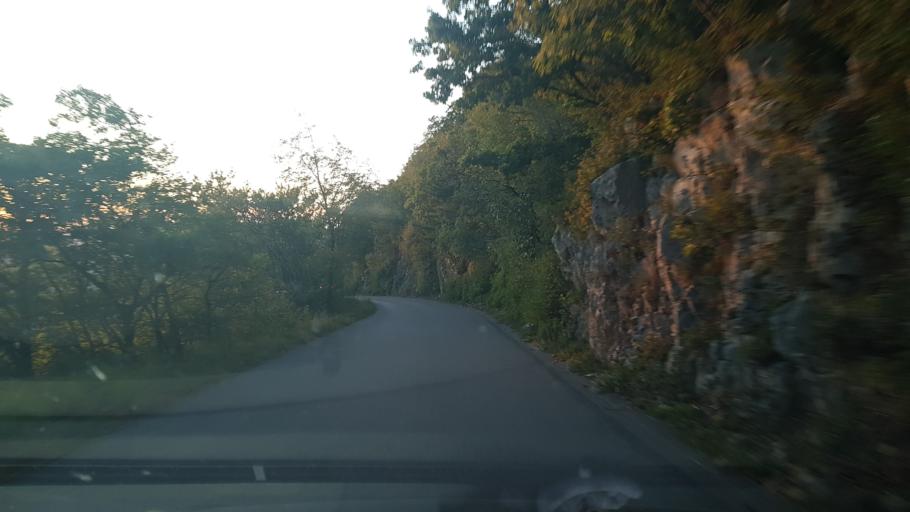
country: SI
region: Vipava
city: Vipava
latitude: 45.7992
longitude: 13.9995
